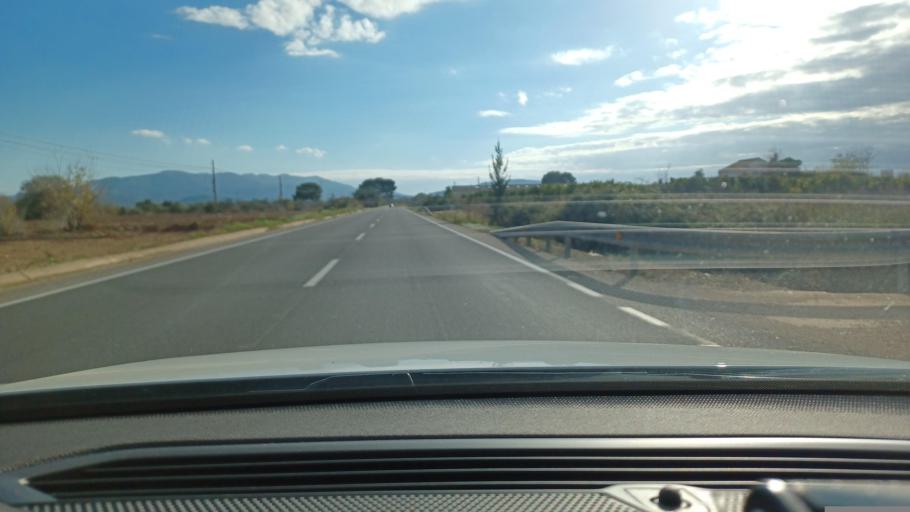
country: ES
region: Catalonia
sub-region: Provincia de Tarragona
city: Santa Barbara
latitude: 40.7299
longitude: 0.5031
